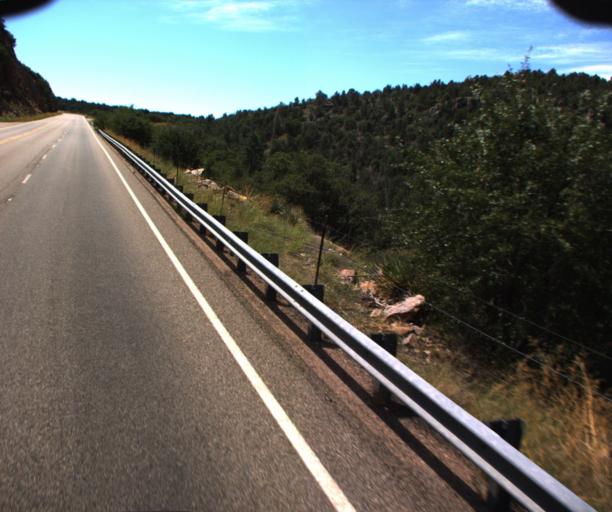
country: US
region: Arizona
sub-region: Navajo County
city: Cibecue
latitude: 33.7382
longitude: -110.5281
